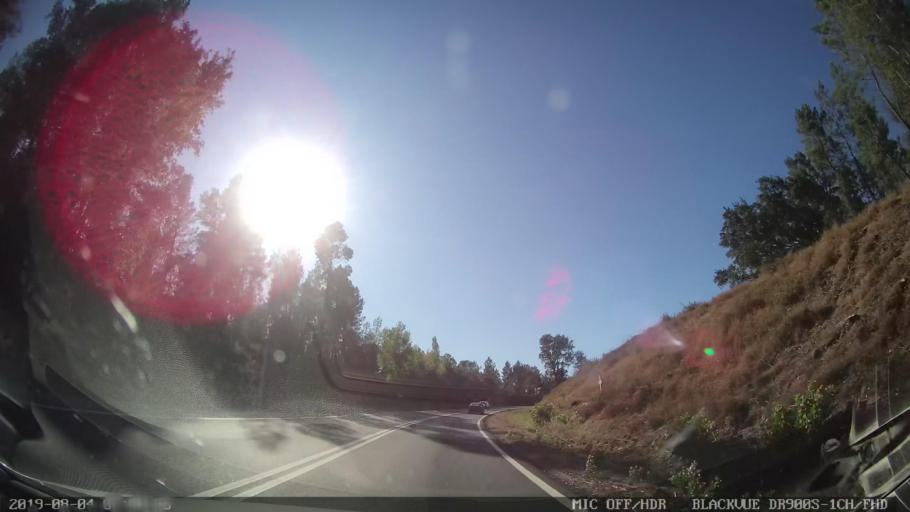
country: PT
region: Santarem
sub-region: Abrantes
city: Alferrarede
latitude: 39.4724
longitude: -8.0702
